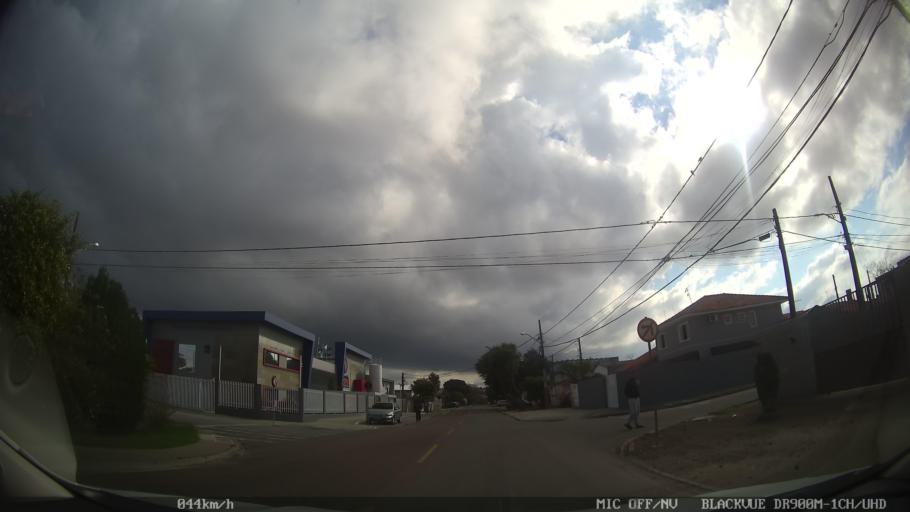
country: BR
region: Parana
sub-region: Pinhais
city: Pinhais
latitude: -25.4038
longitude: -49.1873
